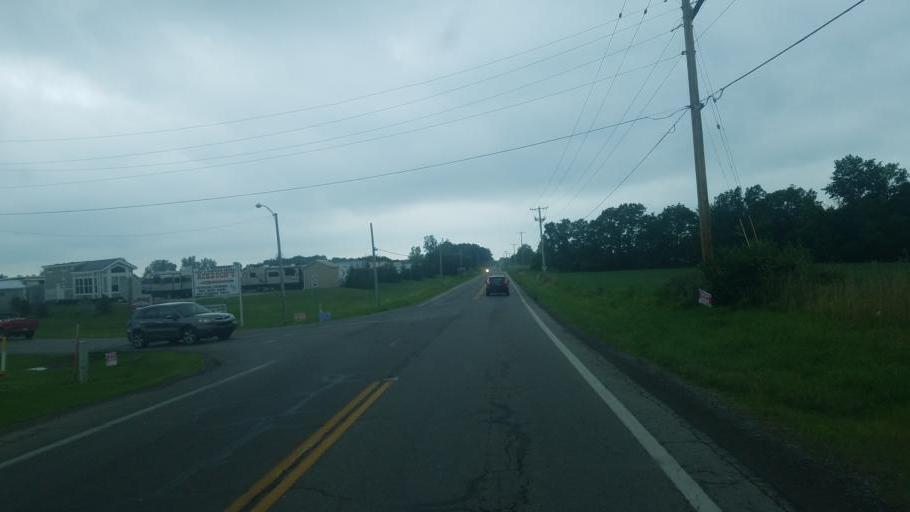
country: US
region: Ohio
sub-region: Logan County
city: Russells Point
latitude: 40.5250
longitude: -83.8617
